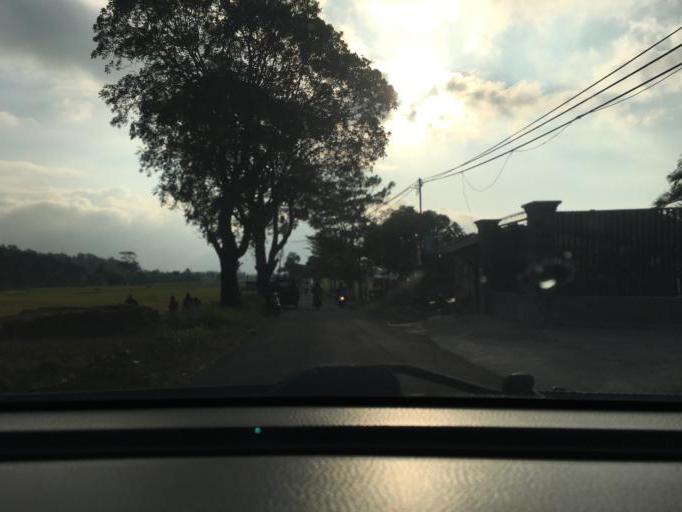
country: ID
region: West Java
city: Nagarakembang
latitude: -7.0359
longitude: 108.3334
